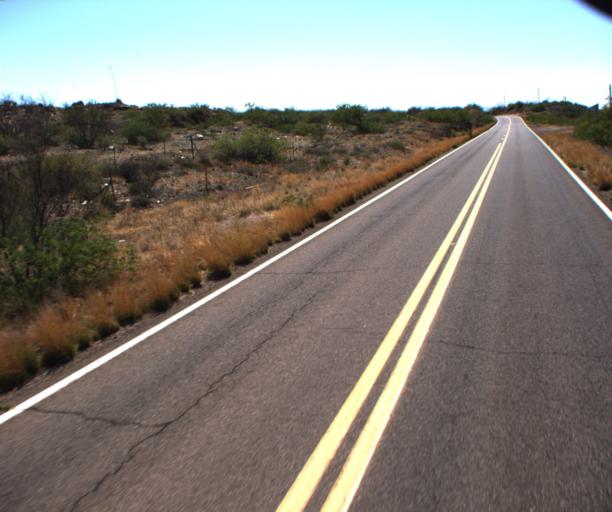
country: US
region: Arizona
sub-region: Cochise County
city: Douglas
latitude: 31.4675
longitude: -109.3844
